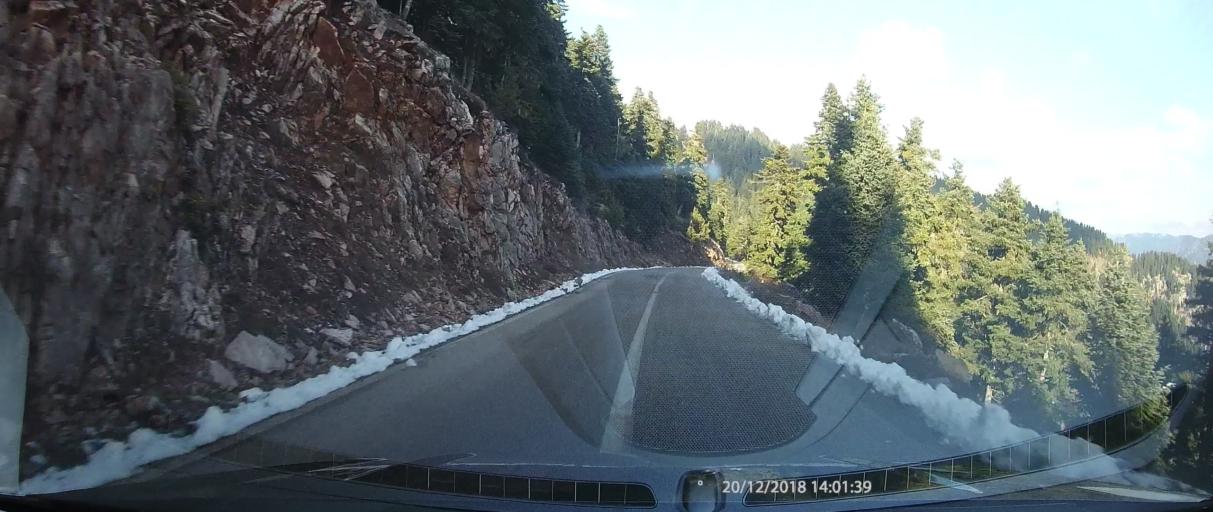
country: GR
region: West Greece
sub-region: Nomos Aitolias kai Akarnanias
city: Thermo
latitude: 38.7310
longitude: 21.6327
